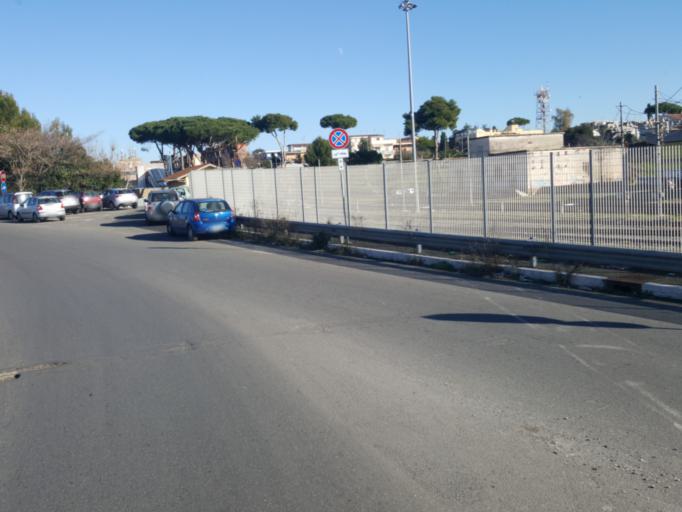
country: IT
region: Latium
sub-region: Citta metropolitana di Roma Capitale
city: Acilia-Castel Fusano-Ostia Antica
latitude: 41.7826
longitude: 12.3575
